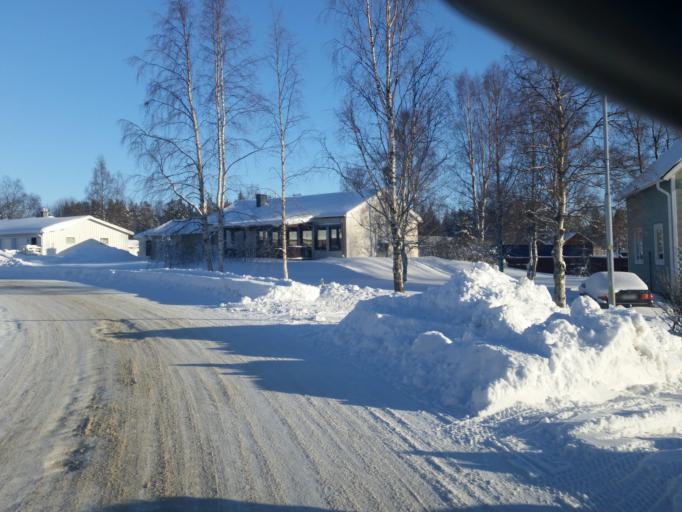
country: SE
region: Norrbotten
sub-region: Pitea Kommun
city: Pitea
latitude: 65.1553
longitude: 21.4912
